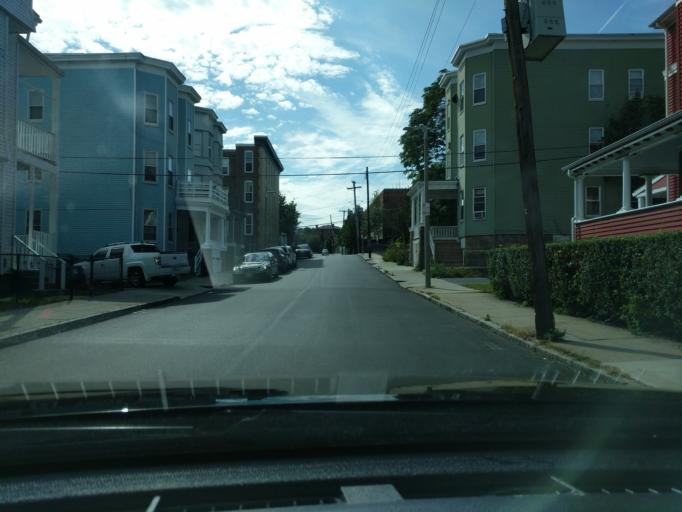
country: US
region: Massachusetts
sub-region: Suffolk County
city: South Boston
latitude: 42.3099
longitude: -71.0797
